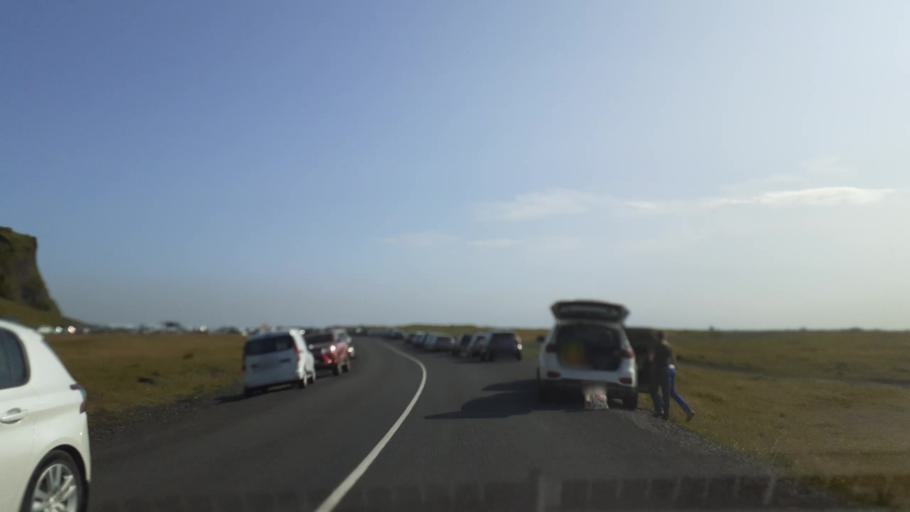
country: IS
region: South
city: Vestmannaeyjar
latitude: 63.4056
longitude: -19.0481
